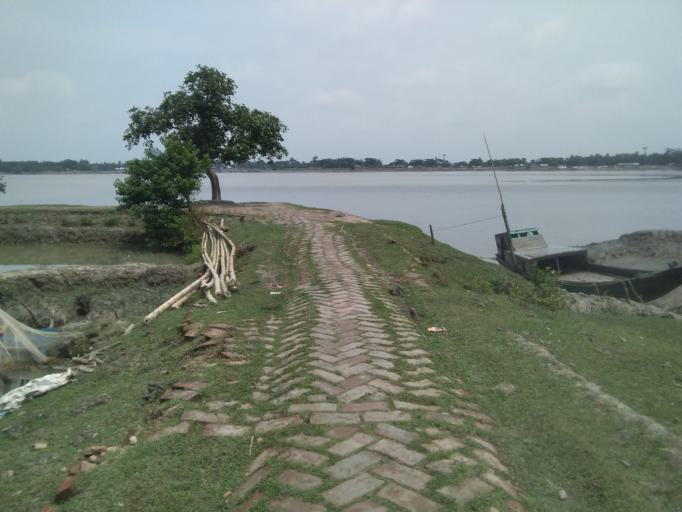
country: BD
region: Khulna
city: Phultala
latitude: 22.6424
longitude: 89.4192
